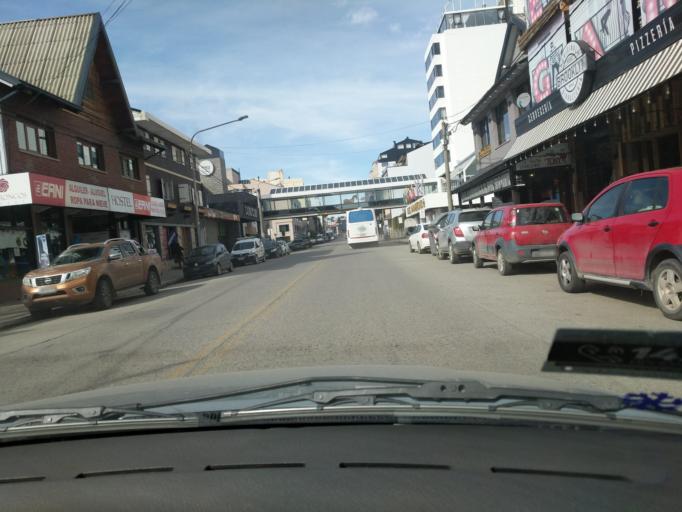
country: AR
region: Rio Negro
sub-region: Departamento de Bariloche
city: San Carlos de Bariloche
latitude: -41.1334
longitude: -71.3177
